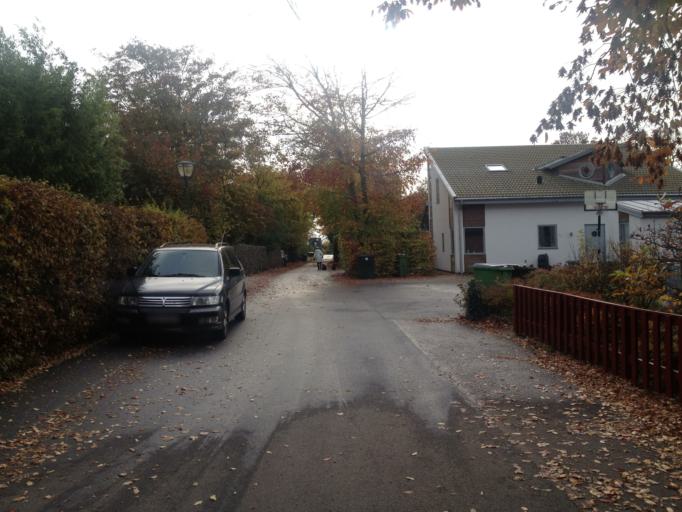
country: SE
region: Skane
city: Bjarred
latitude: 55.7199
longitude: 13.0128
